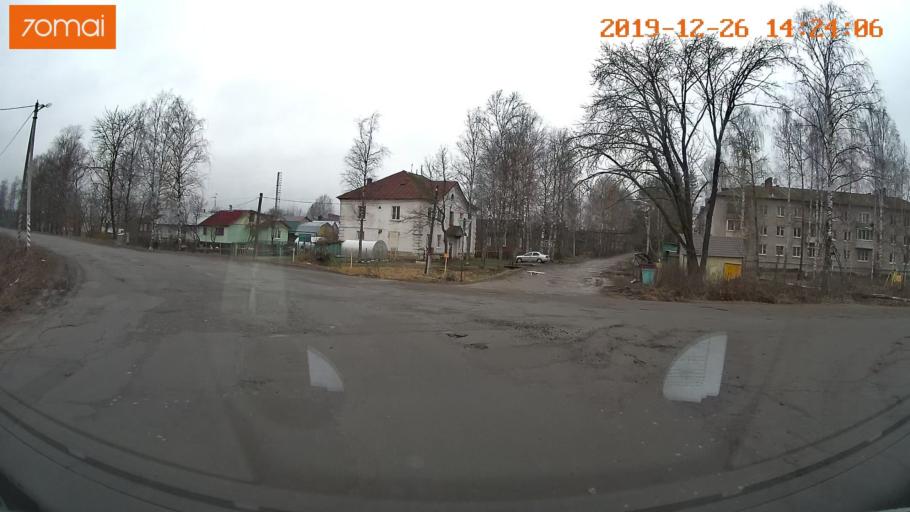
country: RU
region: Jaroslavl
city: Poshekhon'ye
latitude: 58.4992
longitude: 39.1099
